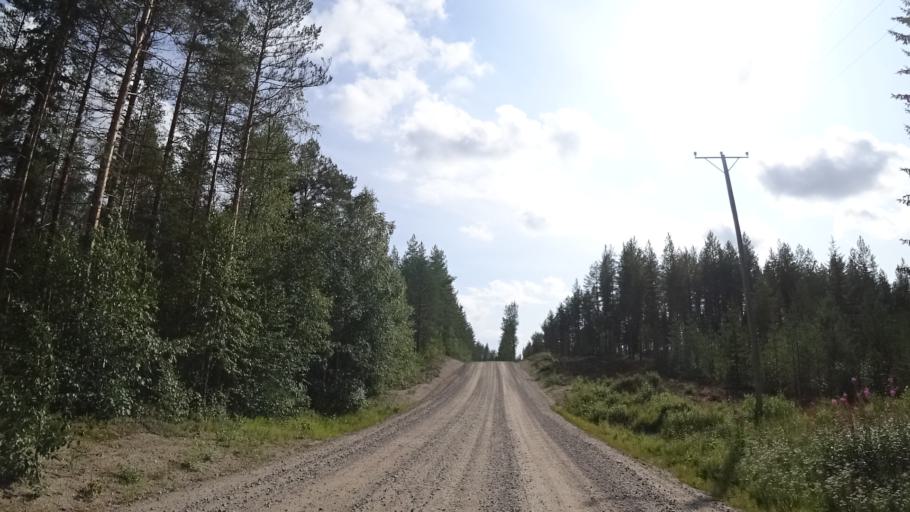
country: FI
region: North Karelia
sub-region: Pielisen Karjala
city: Lieksa
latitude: 63.5583
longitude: 30.0657
